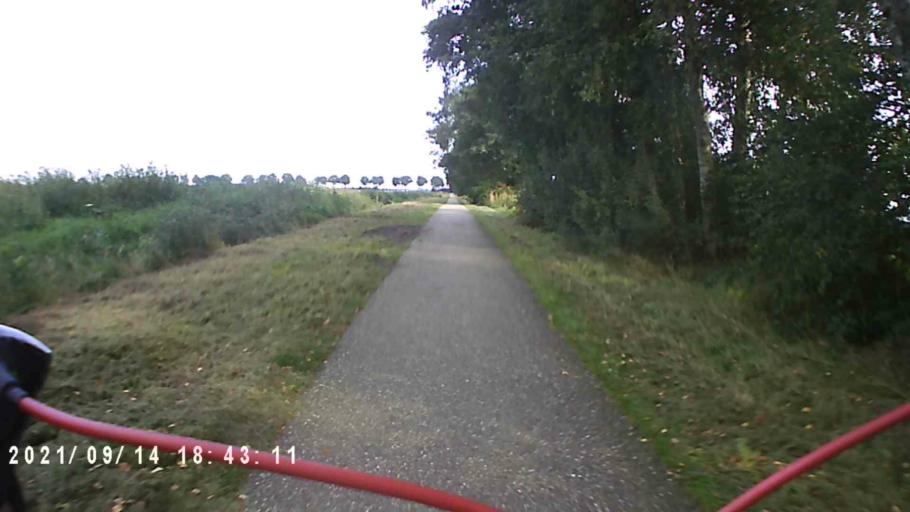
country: NL
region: Drenthe
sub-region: Gemeente Aa en Hunze
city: Anloo
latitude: 53.0237
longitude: 6.6826
